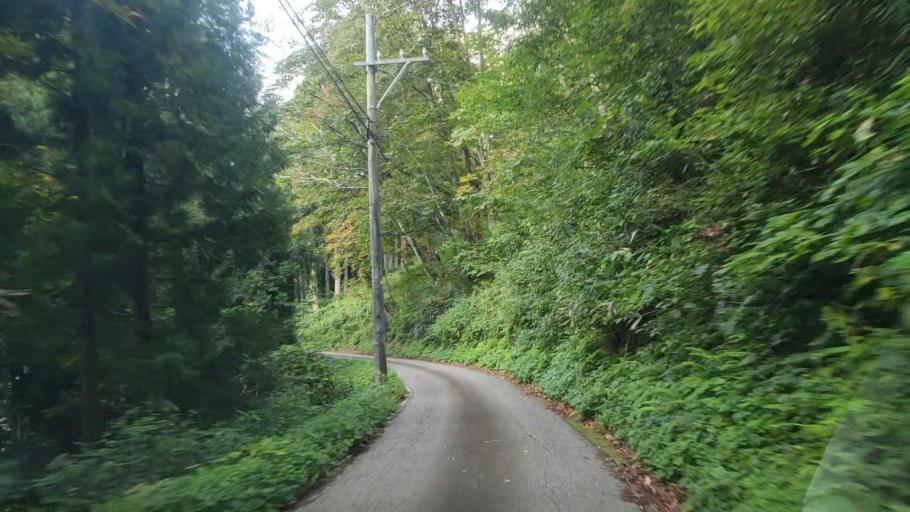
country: JP
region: Toyama
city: Yatsuomachi-higashikumisaka
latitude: 36.4285
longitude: 137.0822
